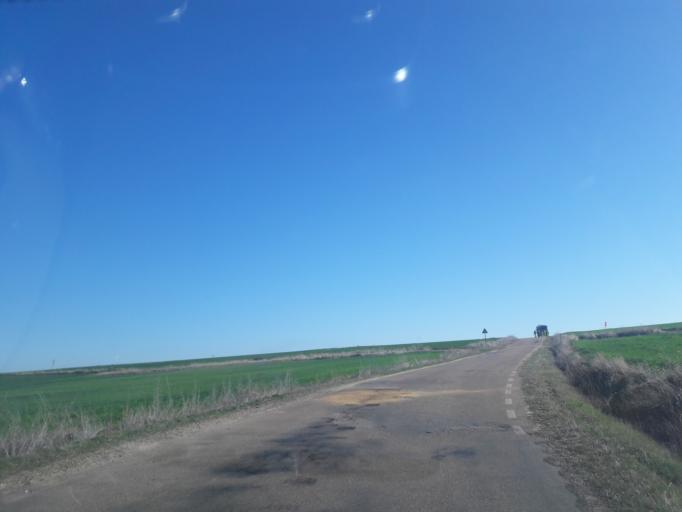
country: ES
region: Castille and Leon
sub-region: Provincia de Salamanca
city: Tordillos
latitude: 40.8761
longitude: -5.3290
